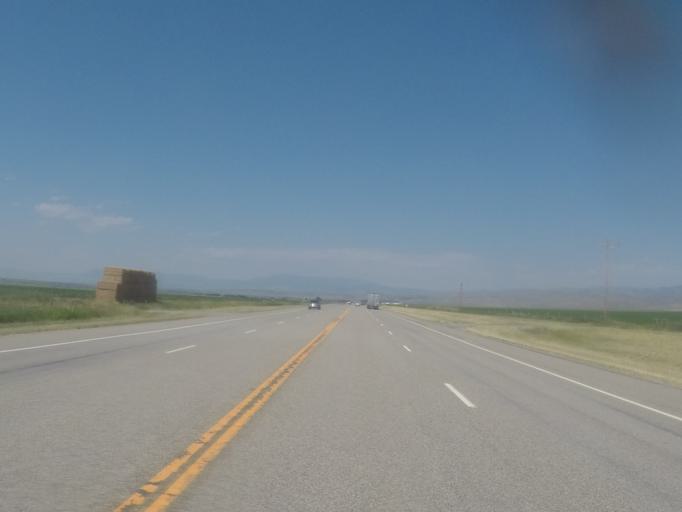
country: US
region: Montana
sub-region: Broadwater County
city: Townsend
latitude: 46.1126
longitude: -111.5056
